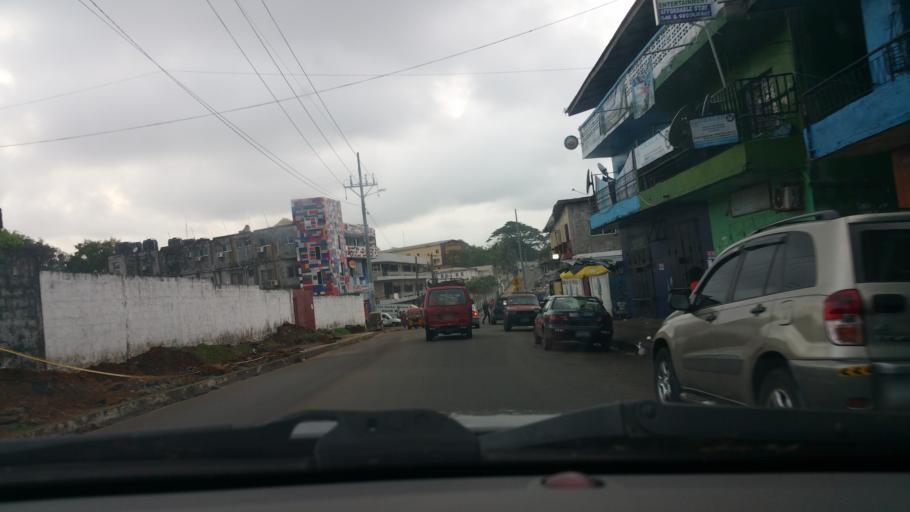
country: LR
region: Montserrado
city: Monrovia
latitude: 6.3066
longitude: -10.7990
